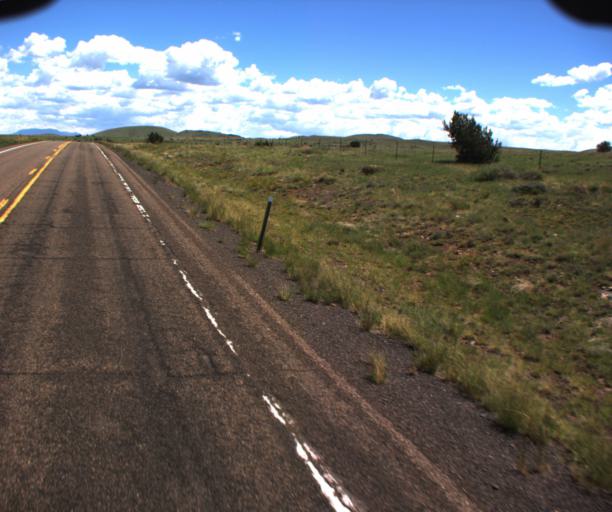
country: US
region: Arizona
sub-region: Apache County
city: Springerville
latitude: 34.2268
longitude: -109.4896
